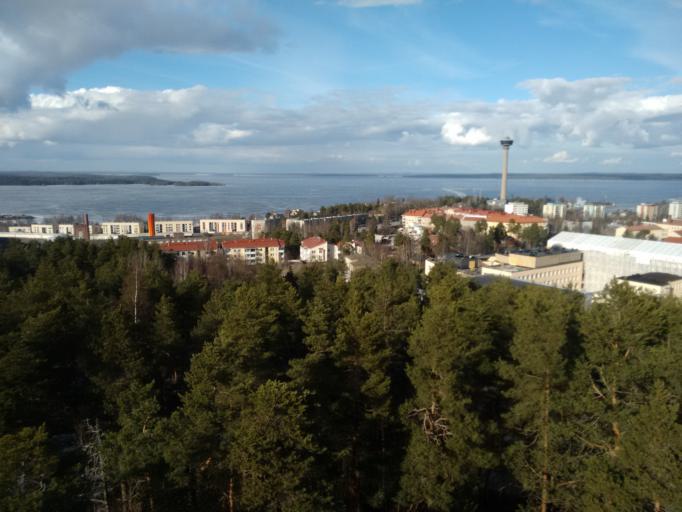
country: FI
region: Pirkanmaa
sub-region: Tampere
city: Tampere
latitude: 61.4979
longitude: 23.7405
